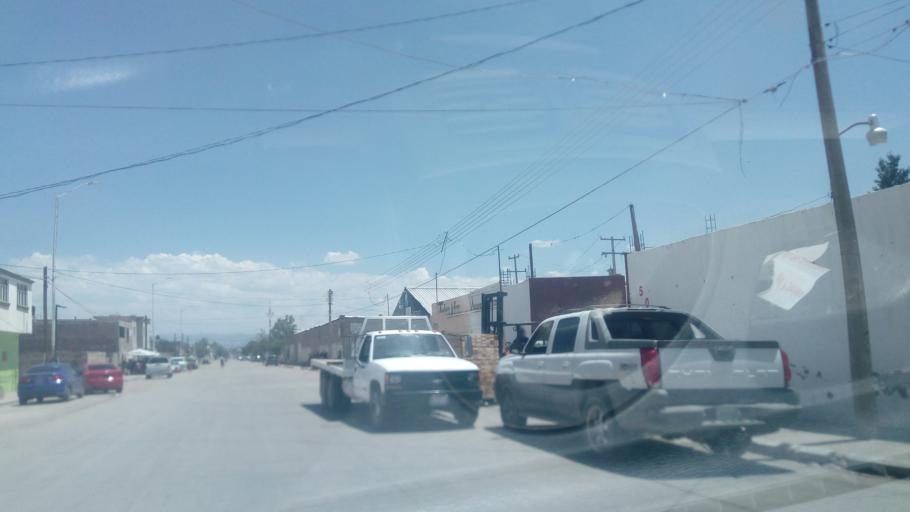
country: MX
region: Durango
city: Victoria de Durango
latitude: 24.0159
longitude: -104.6288
